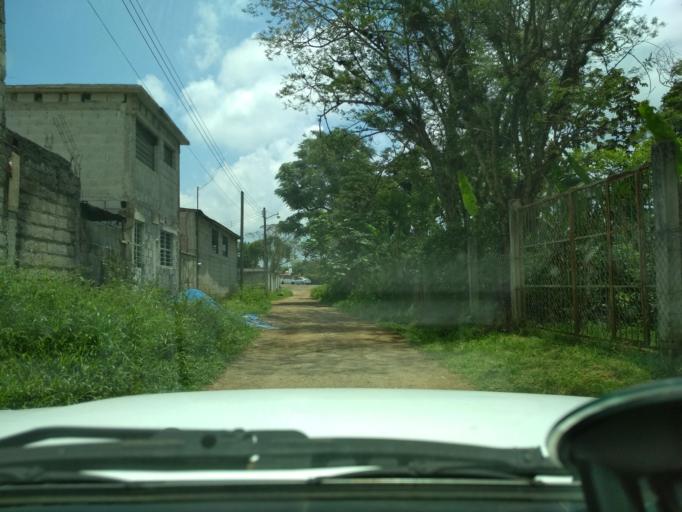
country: MX
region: Veracruz
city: Tocuila
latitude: 18.9506
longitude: -97.0186
